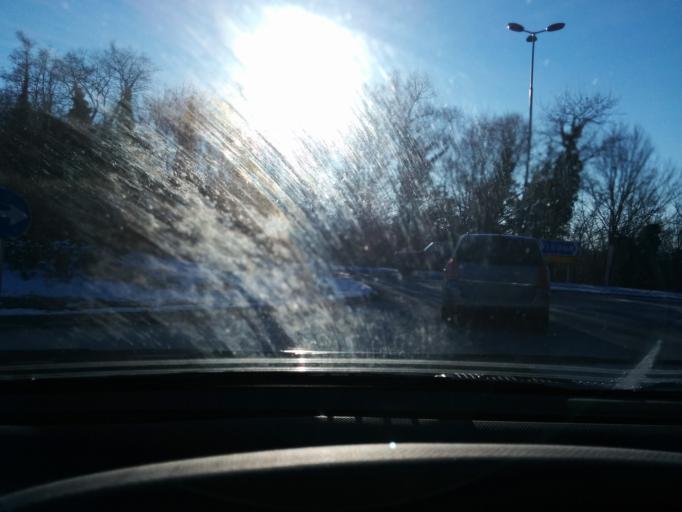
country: AT
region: Styria
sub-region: Politischer Bezirk Graz-Umgebung
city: Nestelbach bei Graz
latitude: 47.0588
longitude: 15.5984
